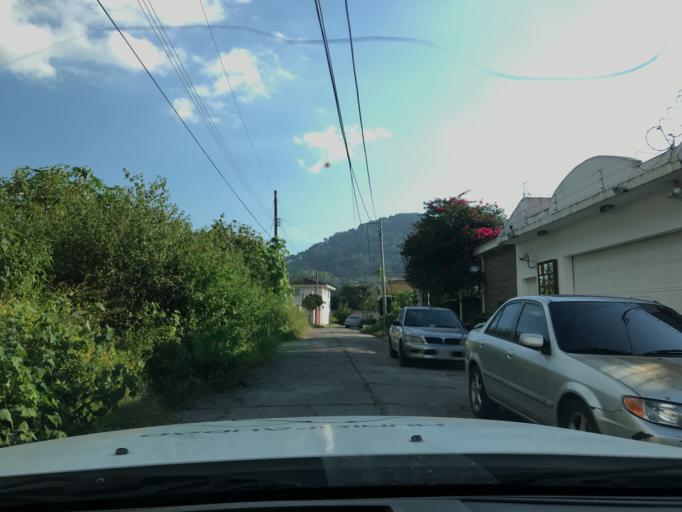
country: GT
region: Guatemala
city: Petapa
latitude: 14.4922
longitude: -90.5462
